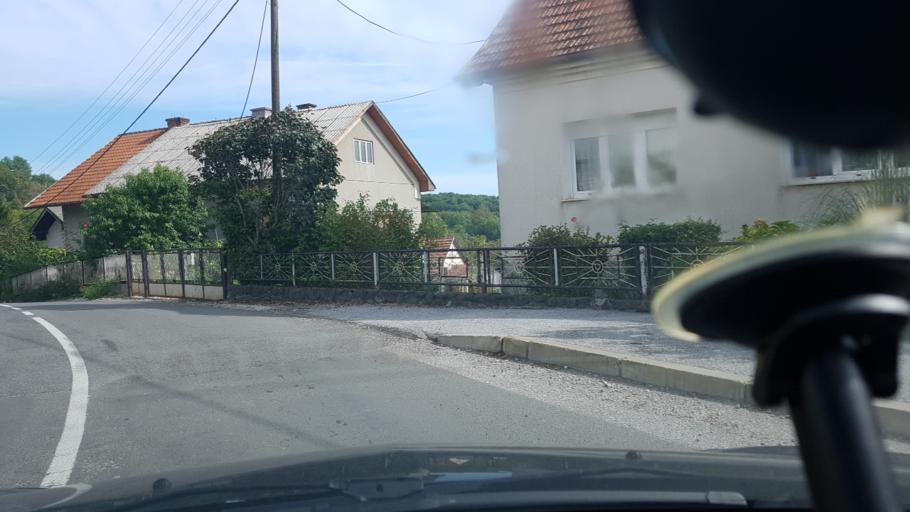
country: HR
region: Varazdinska
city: Remetinec
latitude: 46.1107
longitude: 16.2270
